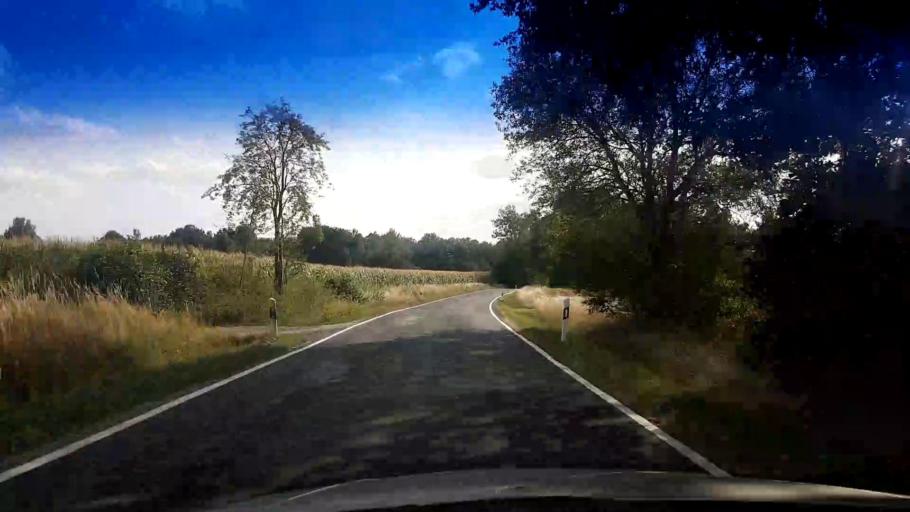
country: DE
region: Bavaria
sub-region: Upper Palatinate
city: Tirschenreuth
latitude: 49.9132
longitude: 12.3921
